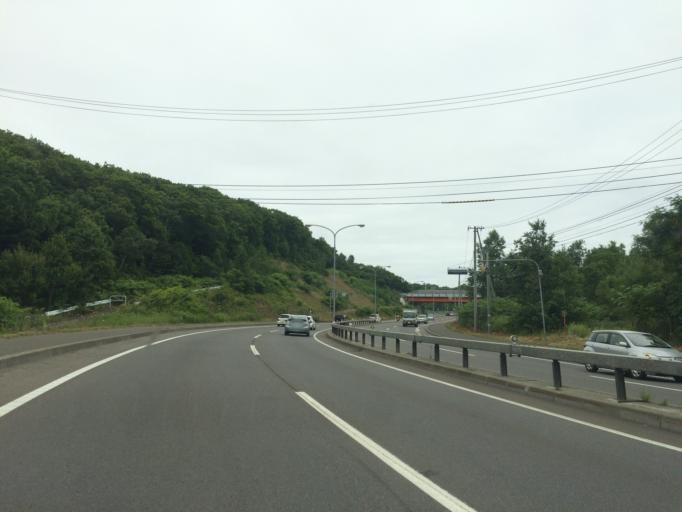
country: JP
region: Hokkaido
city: Otaru
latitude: 43.1542
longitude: 141.1095
